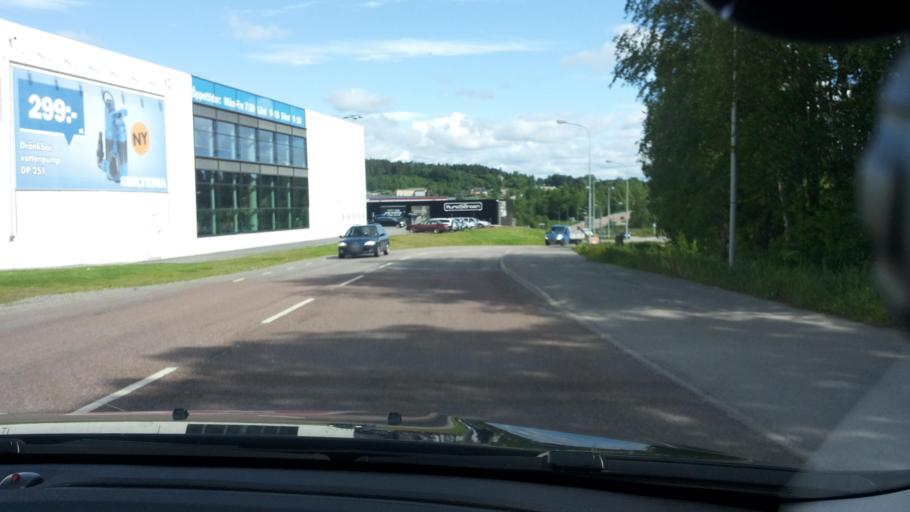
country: SE
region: Vaesternorrland
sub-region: Sundsvalls Kommun
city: Sundsbruk
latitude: 62.4421
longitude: 17.3402
